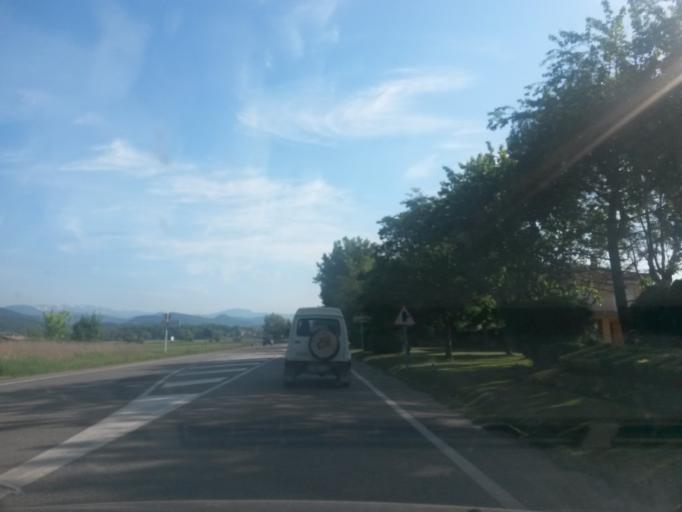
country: ES
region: Catalonia
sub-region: Provincia de Girona
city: Bas
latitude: 42.1486
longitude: 2.4610
